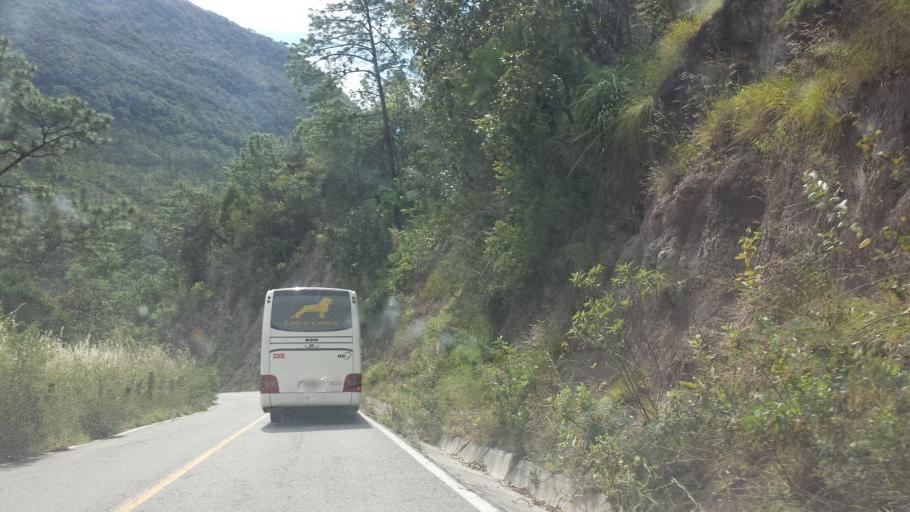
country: MX
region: Oaxaca
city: San Francisco Sola
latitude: 16.4500
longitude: -97.0328
